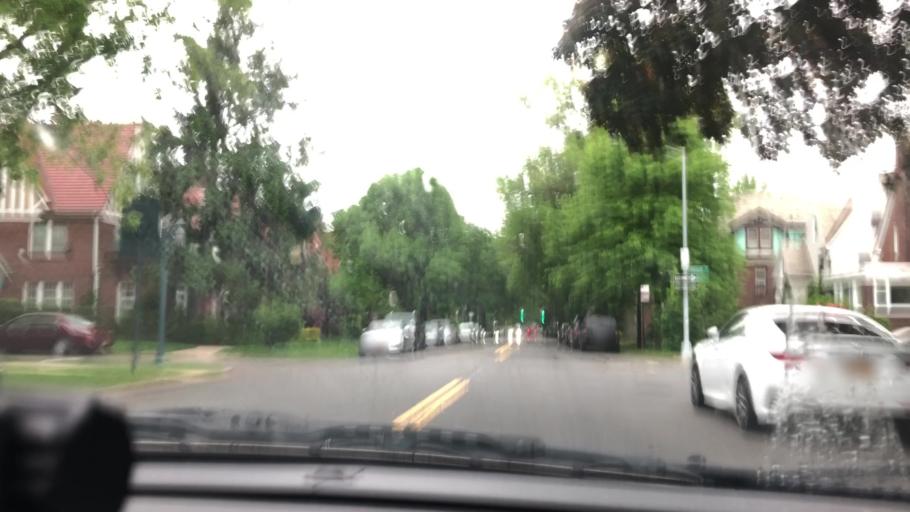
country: US
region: New York
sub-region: Queens County
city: Borough of Queens
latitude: 40.7132
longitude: -73.8438
